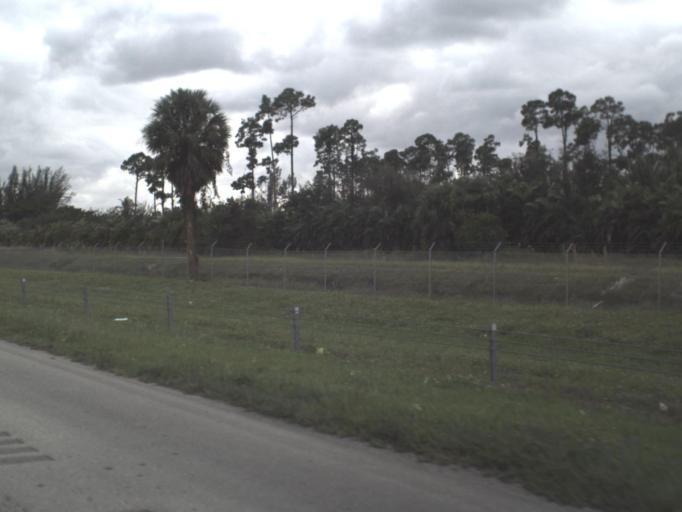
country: US
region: Florida
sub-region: Palm Beach County
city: Lake Belvedere Estates
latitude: 26.6602
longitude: -80.1743
